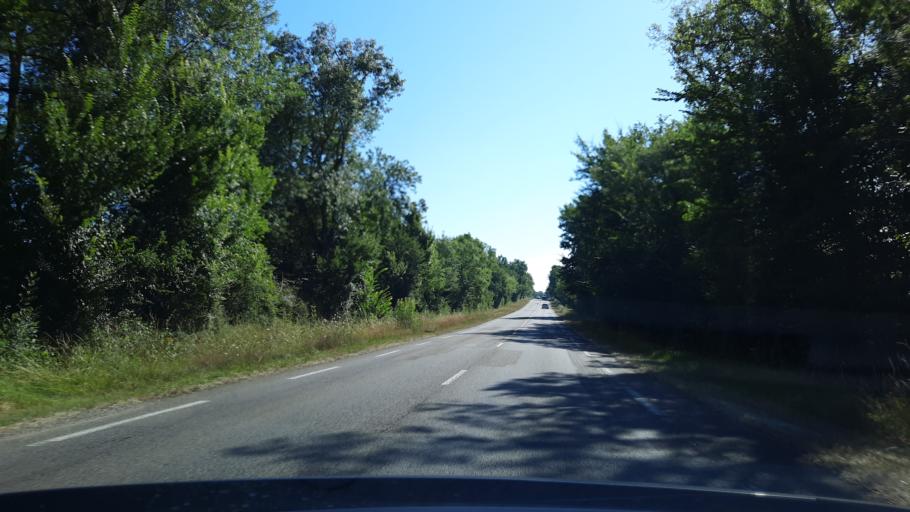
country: FR
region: Midi-Pyrenees
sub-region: Departement du Tarn-et-Garonne
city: Monteils
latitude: 44.1692
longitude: 1.5823
